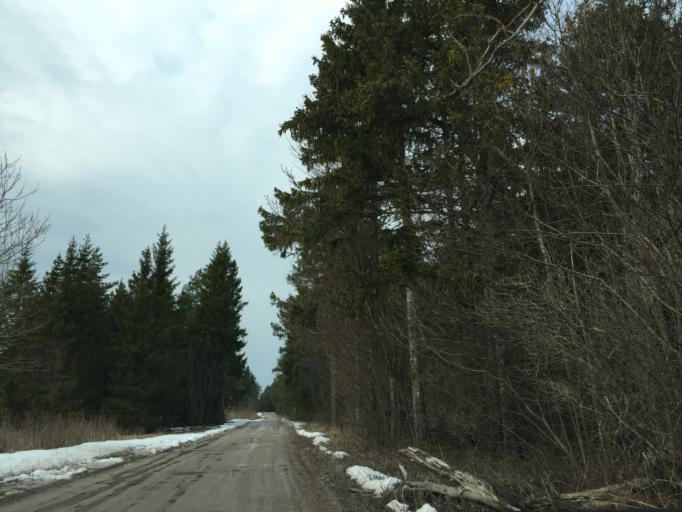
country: EE
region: Saare
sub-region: Kuressaare linn
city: Kuressaare
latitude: 58.4254
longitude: 22.1516
